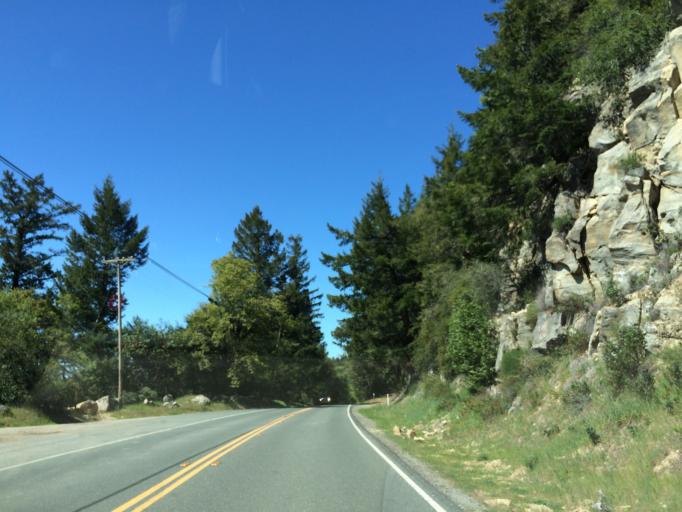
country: US
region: California
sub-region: Santa Clara County
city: Saratoga
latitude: 37.2451
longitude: -122.1099
